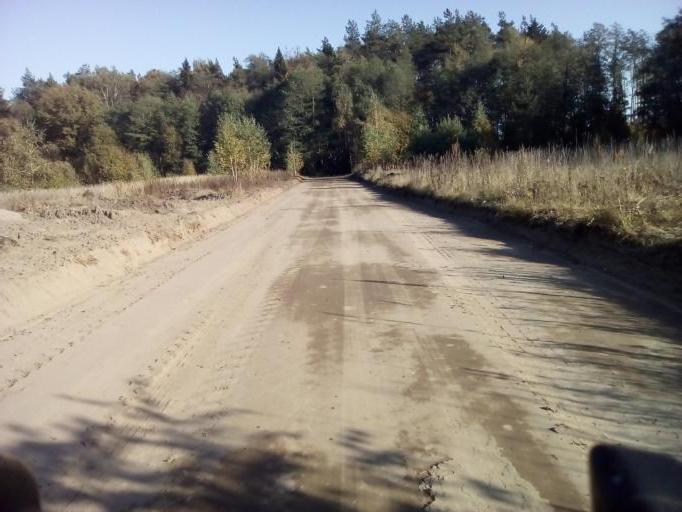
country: RU
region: Moskovskaya
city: Ramenskoye
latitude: 55.5717
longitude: 38.3087
